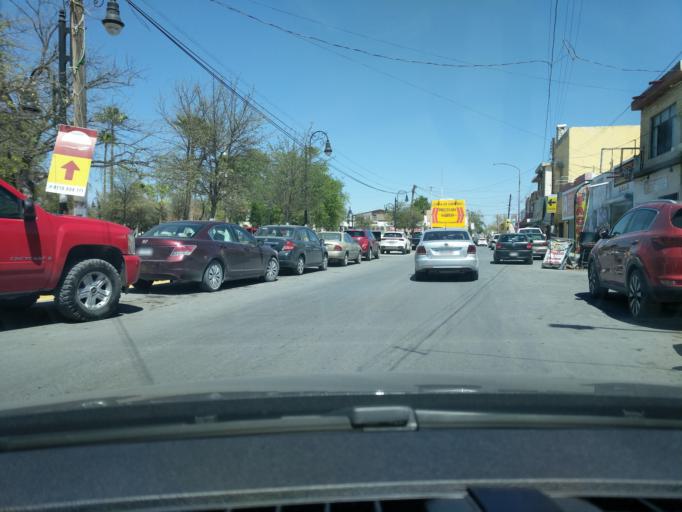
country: MX
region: Nuevo Leon
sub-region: Salinas Victoria
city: Las Torres
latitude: 25.9594
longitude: -100.2911
